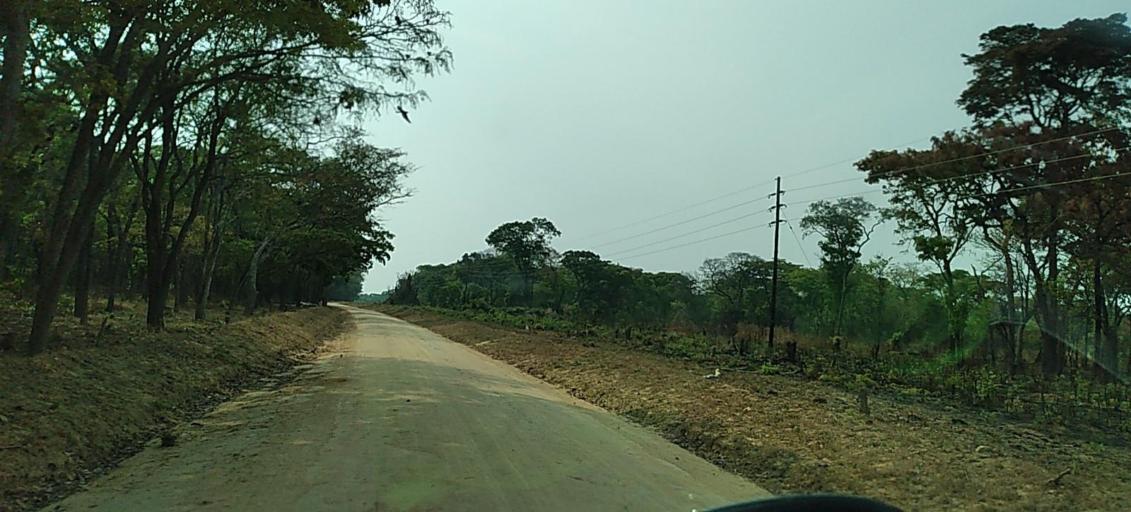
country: ZM
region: North-Western
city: Solwezi
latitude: -12.6921
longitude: 26.4017
